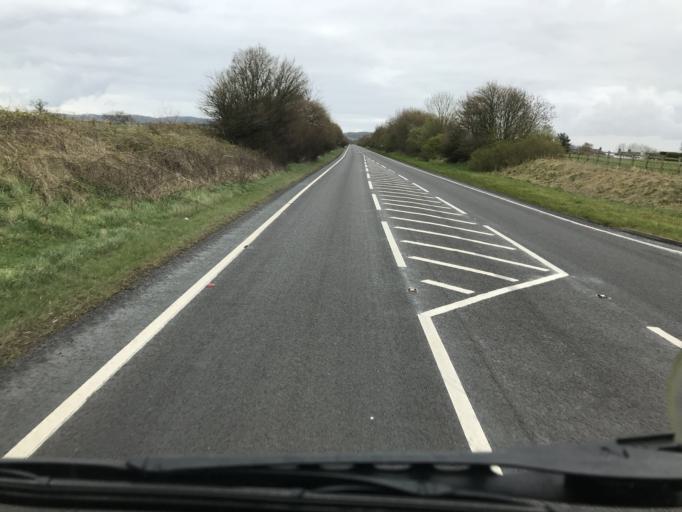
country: GB
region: England
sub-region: Cheshire West and Chester
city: Tattenhall
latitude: 53.1177
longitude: -2.7988
